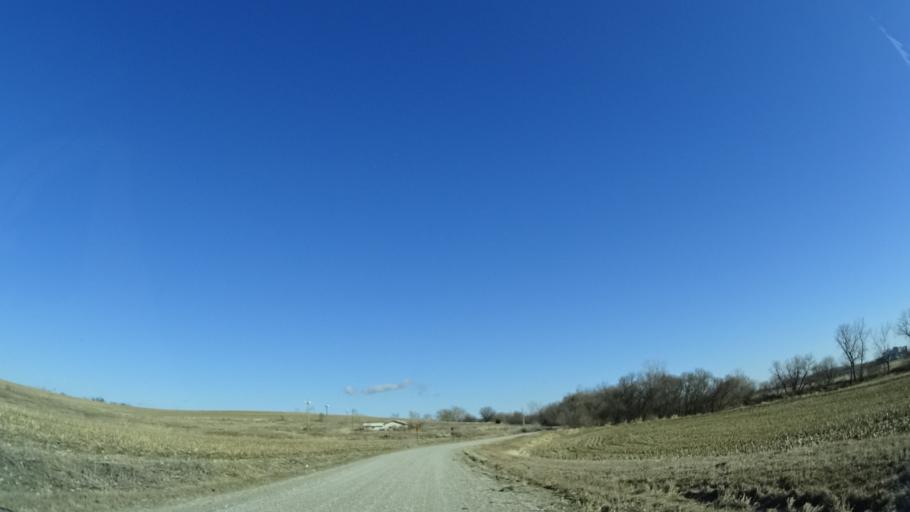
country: US
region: Nebraska
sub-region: Sarpy County
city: Offutt Air Force Base
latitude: 41.1471
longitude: -95.9588
